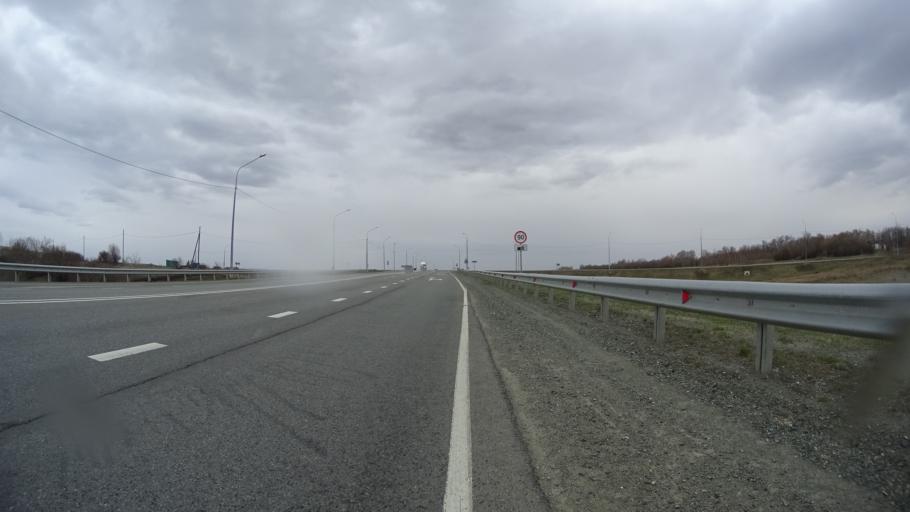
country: RU
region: Chelyabinsk
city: Krasnogorskiy
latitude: 54.6750
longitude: 61.2486
